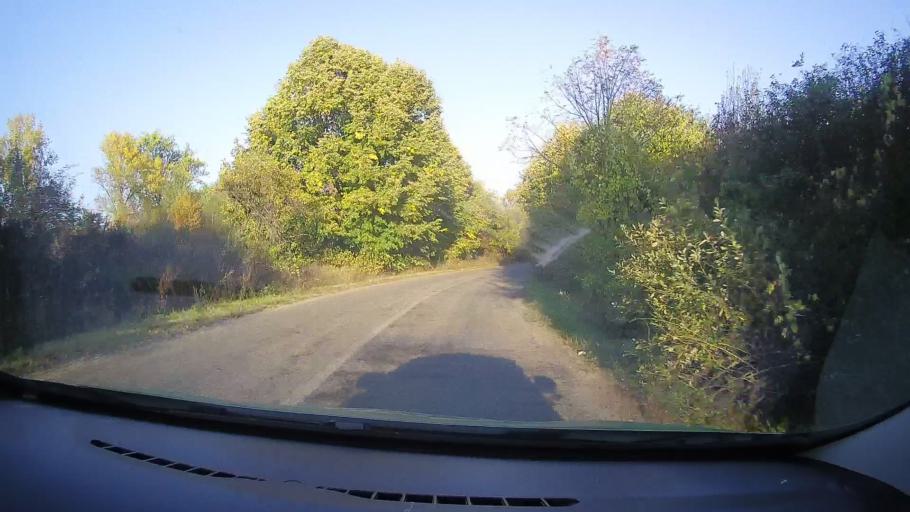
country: RO
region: Arad
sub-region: Comuna Silindia
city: Silindia
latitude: 46.3367
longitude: 21.8805
